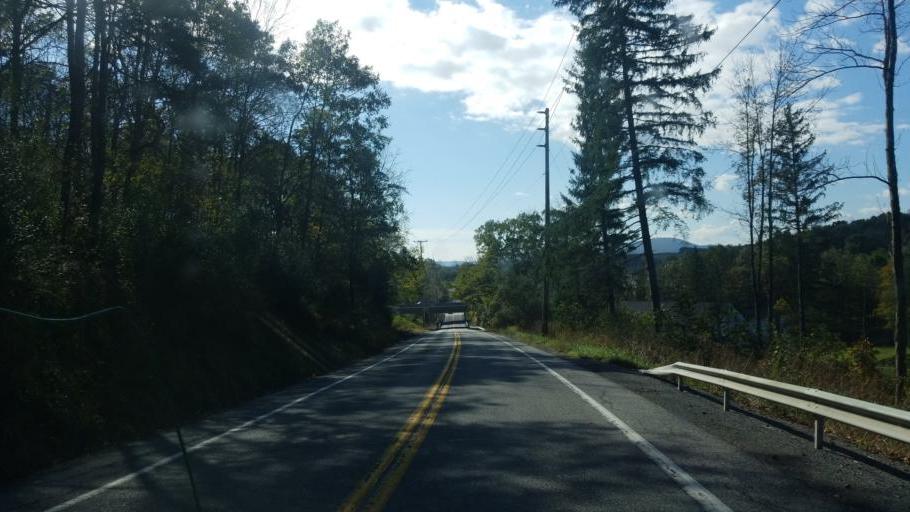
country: US
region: Pennsylvania
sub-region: Bedford County
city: Bedford
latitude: 40.1127
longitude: -78.5265
